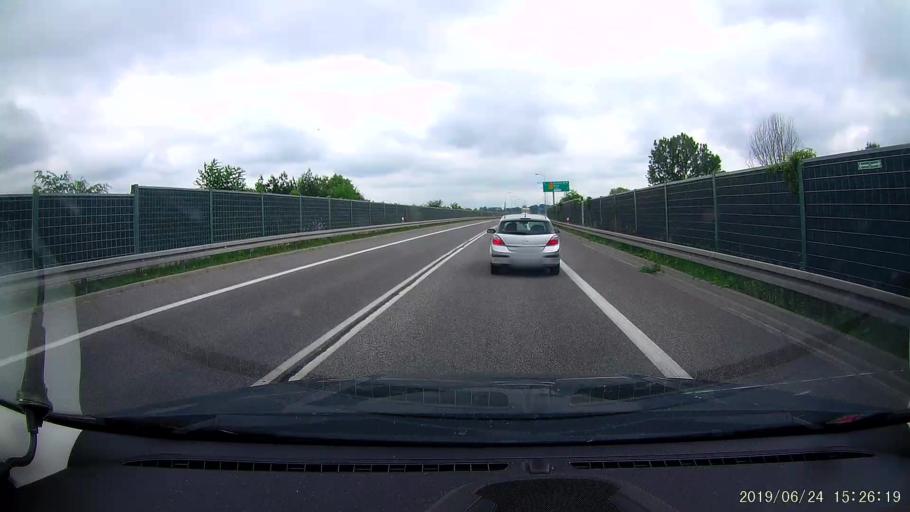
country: PL
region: Subcarpathian Voivodeship
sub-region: Powiat jaroslawski
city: Jaroslaw
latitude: 50.0254
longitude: 22.6932
